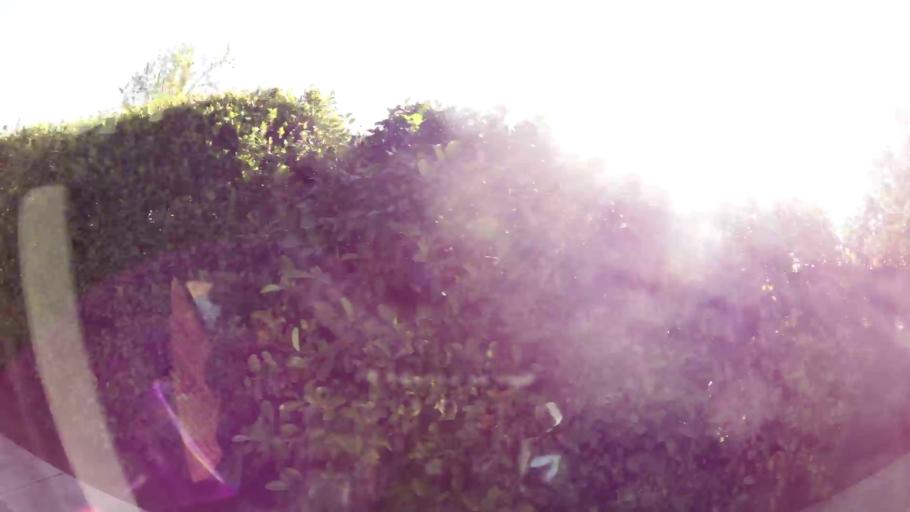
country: CL
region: Santiago Metropolitan
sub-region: Provincia de Santiago
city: Villa Presidente Frei, Nunoa, Santiago, Chile
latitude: -33.3696
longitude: -70.5008
